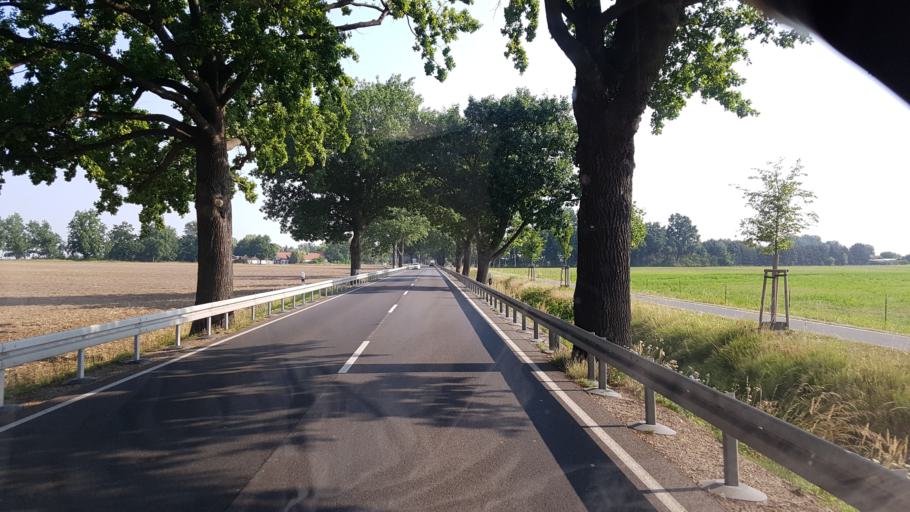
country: DE
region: Brandenburg
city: Kolkwitz
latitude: 51.7071
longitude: 14.2823
